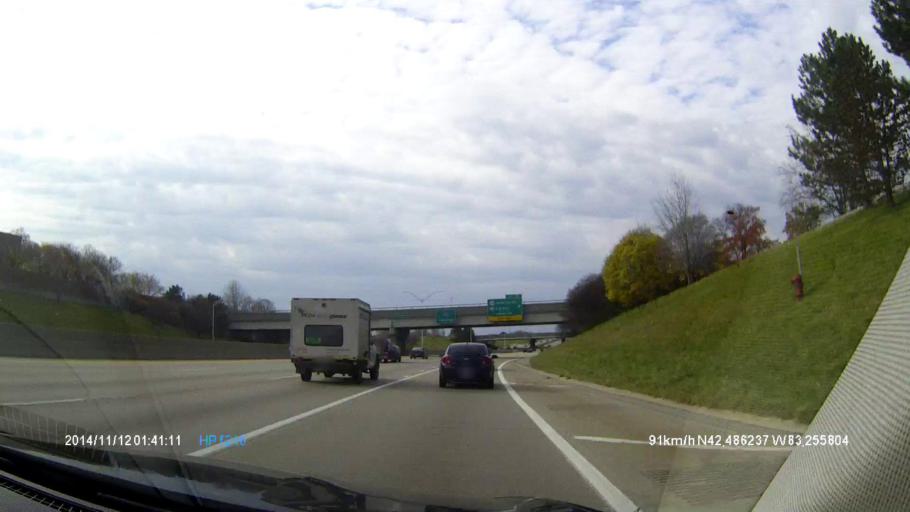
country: US
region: Michigan
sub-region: Oakland County
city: Bingham Farms
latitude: 42.4862
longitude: -83.2559
